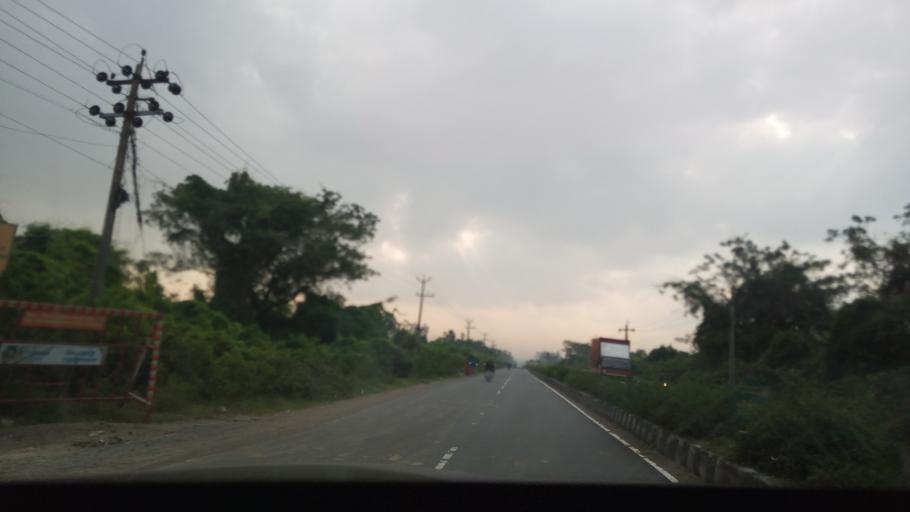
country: IN
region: Tamil Nadu
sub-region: Kancheepuram
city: Vengavasal
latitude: 12.8231
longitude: 80.1700
